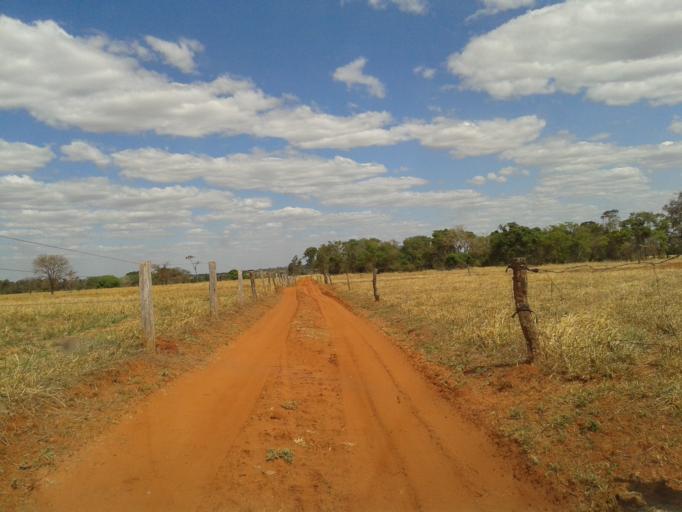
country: BR
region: Minas Gerais
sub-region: Centralina
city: Centralina
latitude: -18.7723
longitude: -49.0902
